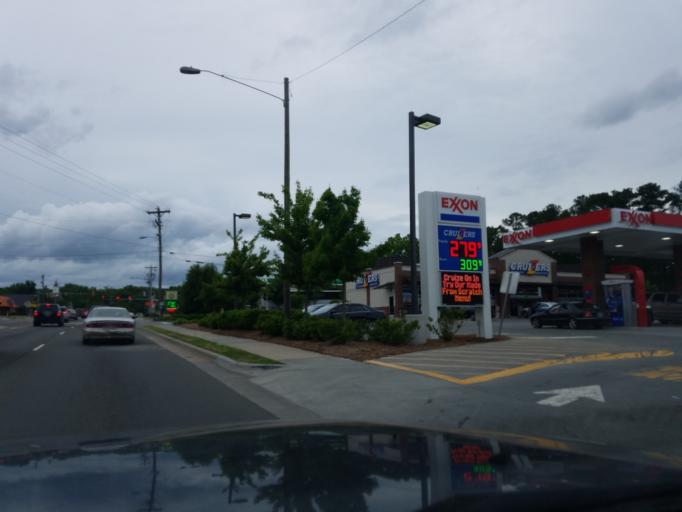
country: US
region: North Carolina
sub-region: Durham County
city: Durham
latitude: 36.0296
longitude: -78.9265
